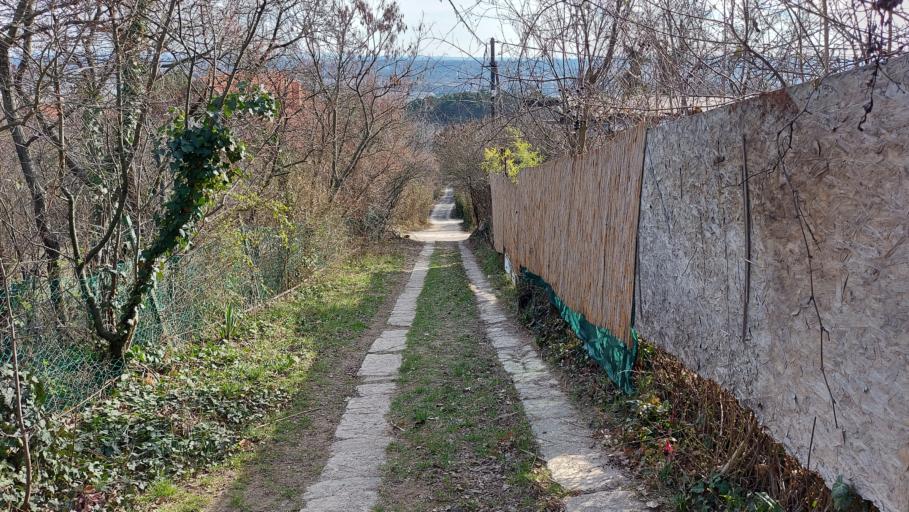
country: HU
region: Pest
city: Budaors
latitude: 47.4742
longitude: 18.9664
